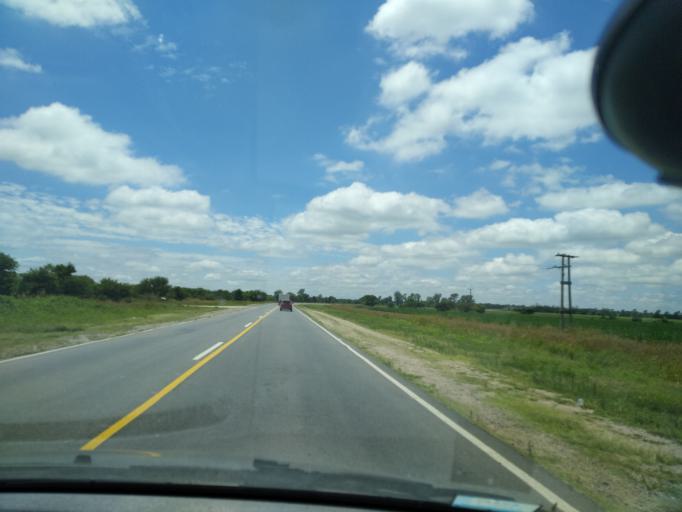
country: AR
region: Cordoba
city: Alta Gracia
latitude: -31.6545
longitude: -64.3502
